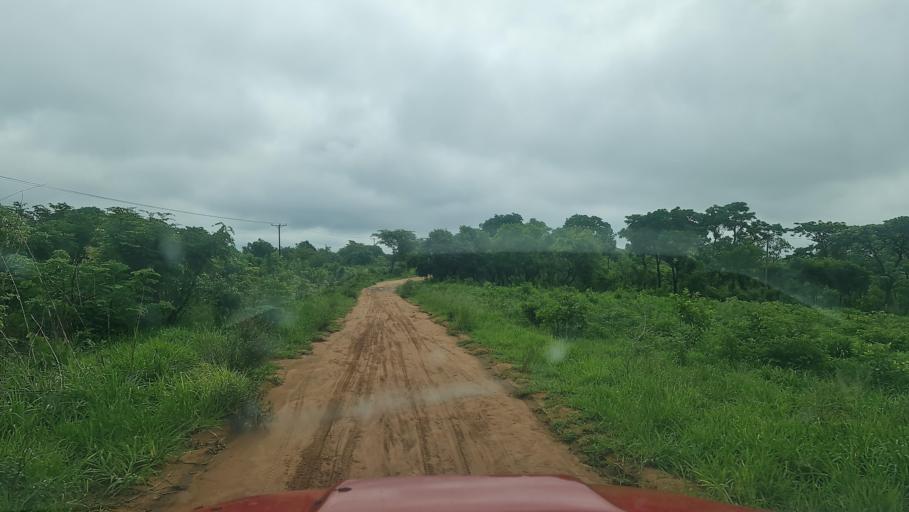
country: MW
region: Southern Region
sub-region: Nsanje District
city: Nsanje
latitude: -17.1928
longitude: 35.8509
